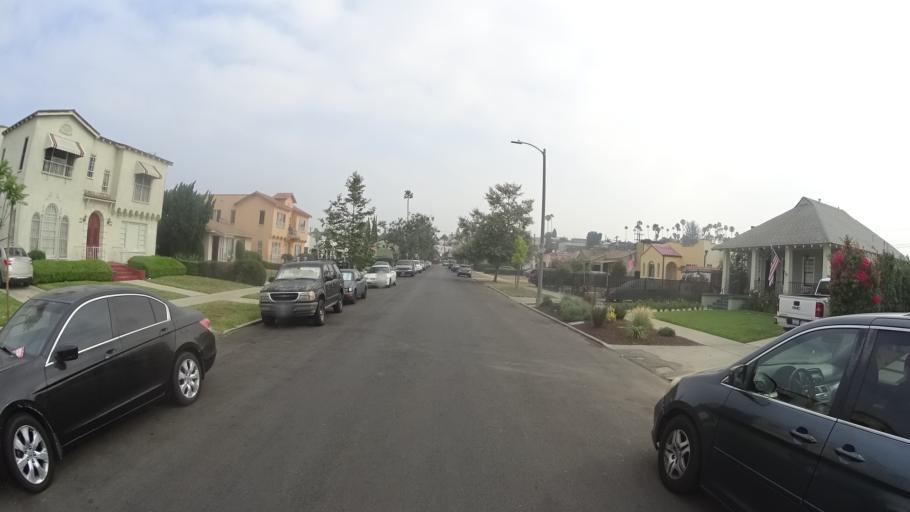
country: US
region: California
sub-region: Los Angeles County
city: View Park-Windsor Hills
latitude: 34.0281
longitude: -118.3282
